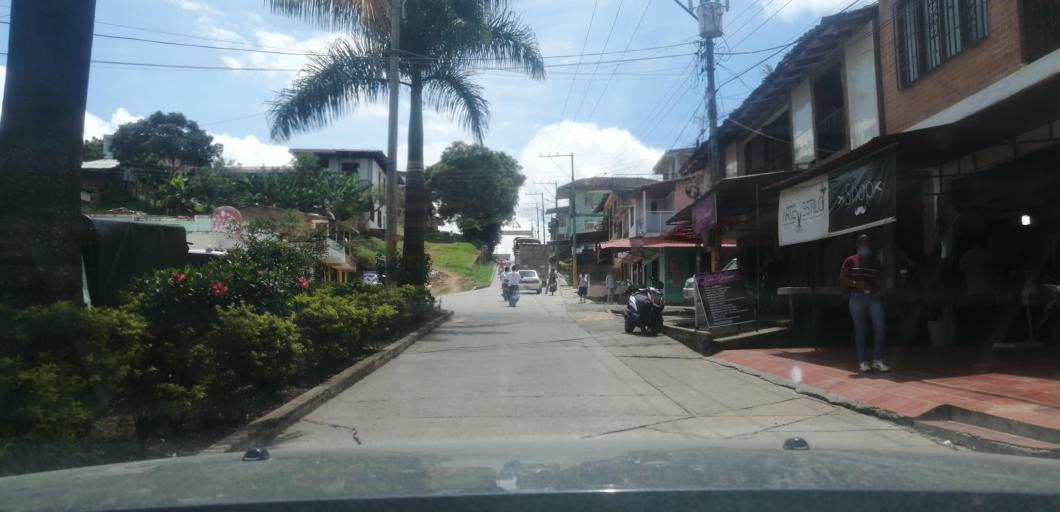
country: CO
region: Valle del Cauca
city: Restrepo
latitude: 3.8238
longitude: -76.5222
